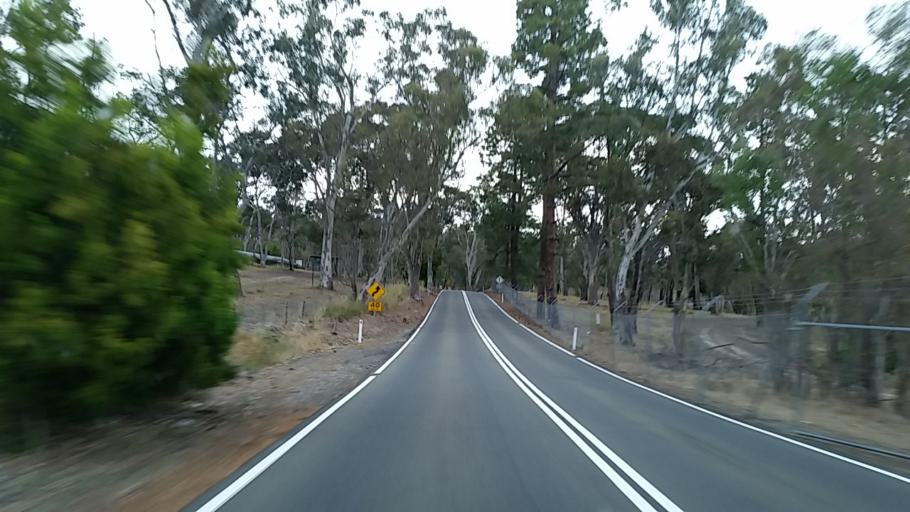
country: AU
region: South Australia
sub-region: Adelaide Hills
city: Gumeracha
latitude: -34.8322
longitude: 138.8241
